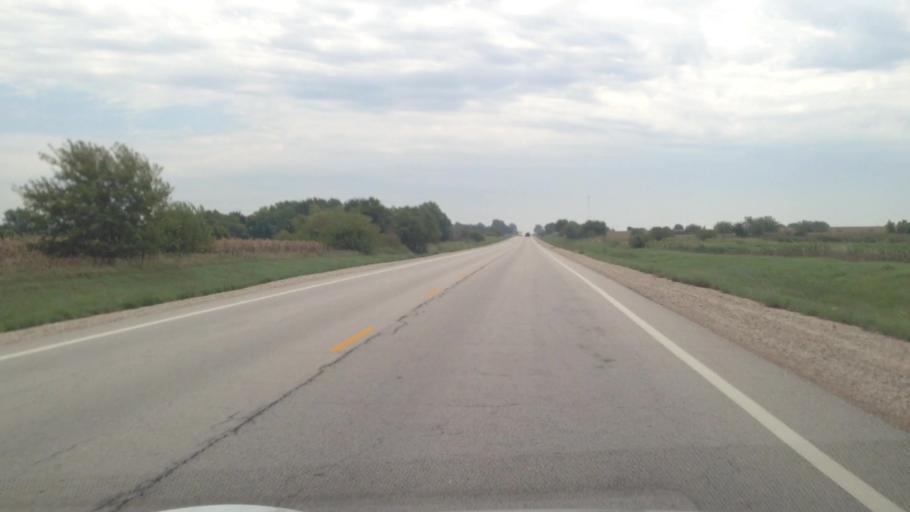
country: US
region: Kansas
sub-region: Anderson County
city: Garnett
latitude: 38.0818
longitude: -95.2001
